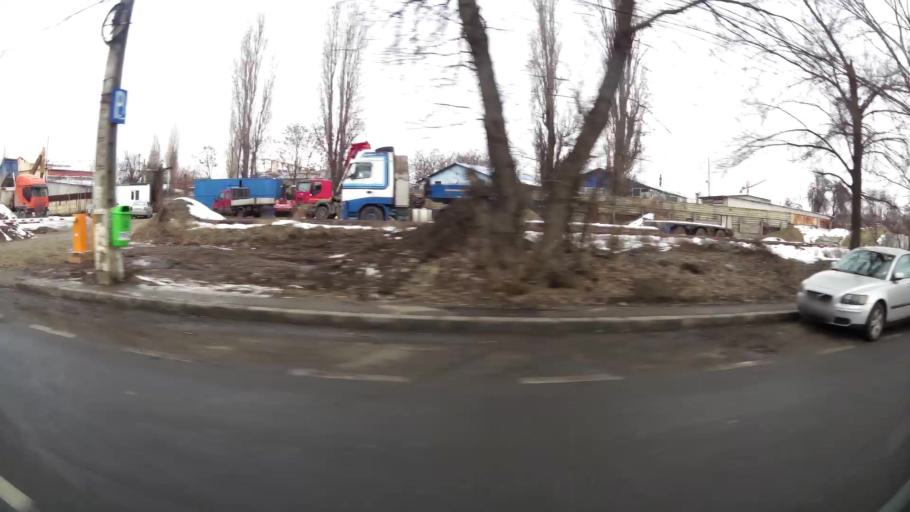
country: RO
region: Ilfov
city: Dobroesti
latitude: 44.4348
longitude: 26.1810
